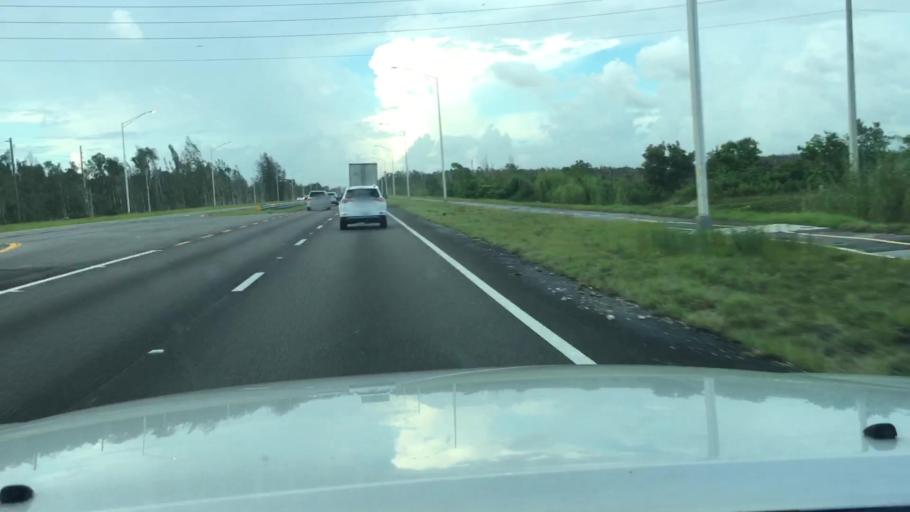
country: US
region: Florida
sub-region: Miami-Dade County
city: Kendall West
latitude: 25.7265
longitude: -80.4799
